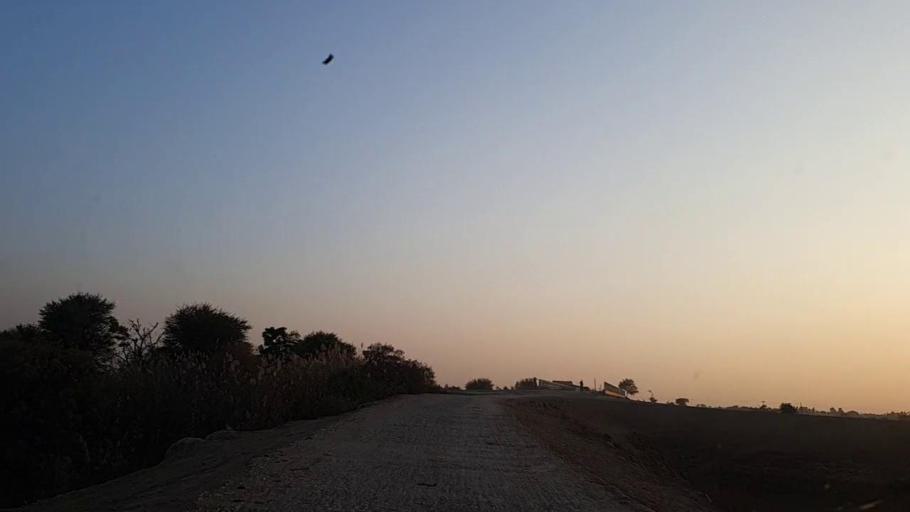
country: PK
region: Sindh
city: Bhit Shah
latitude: 25.9156
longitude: 68.5061
